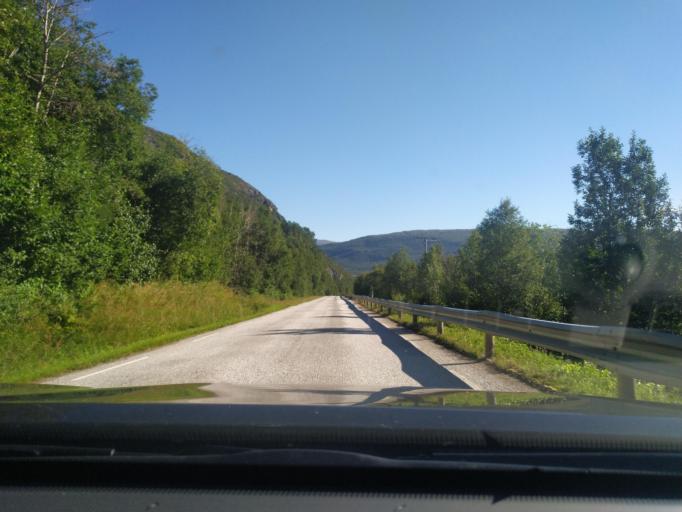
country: NO
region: Troms
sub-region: Dyroy
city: Brostadbotn
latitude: 68.9292
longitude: 17.6507
